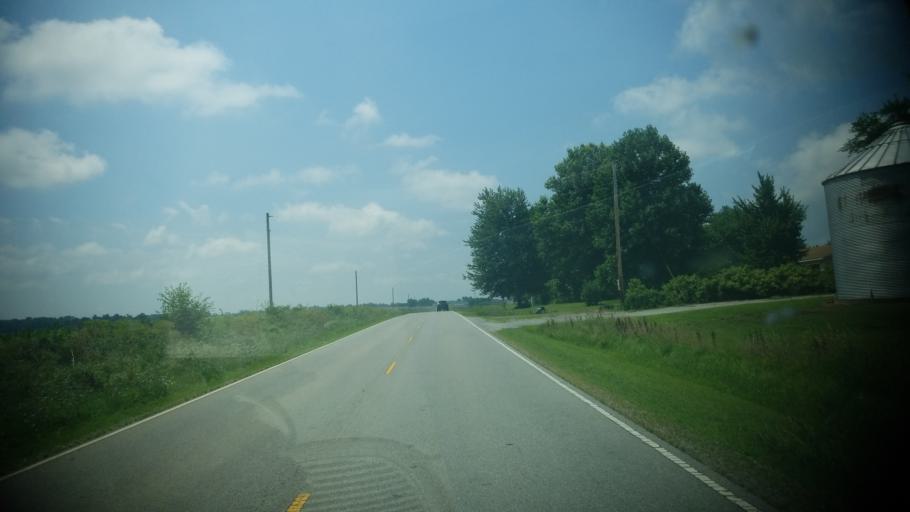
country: US
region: Illinois
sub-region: Wayne County
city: Fairfield
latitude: 38.4546
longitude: -88.3491
